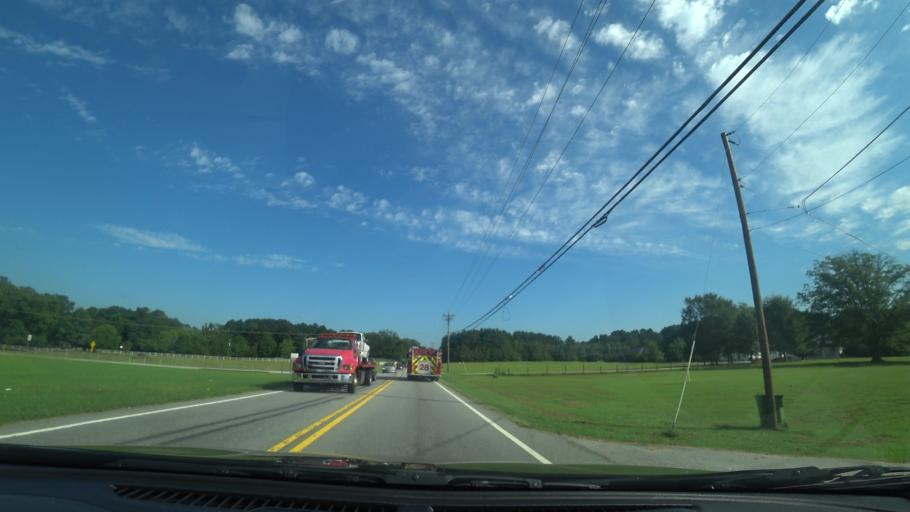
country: US
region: Georgia
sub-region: Gwinnett County
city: Grayson
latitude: 33.8553
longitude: -83.9563
